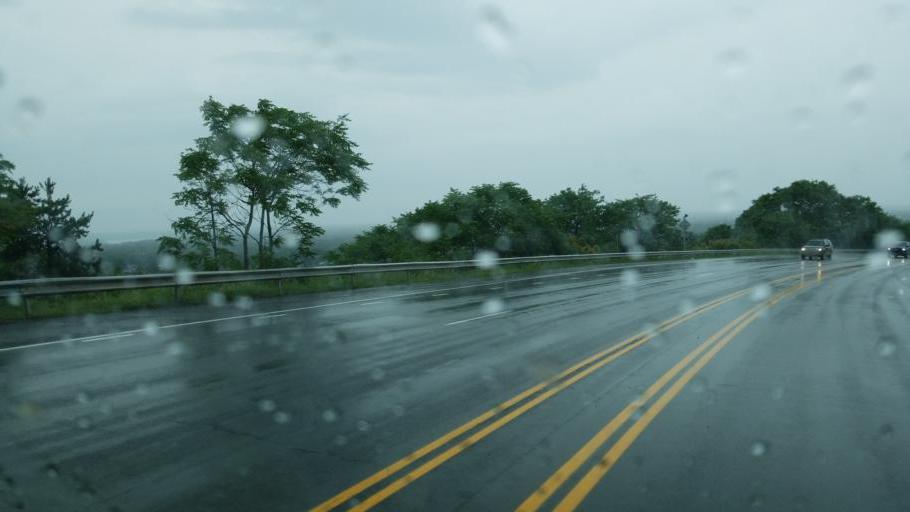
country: US
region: New York
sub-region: Niagara County
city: Lewiston
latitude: 43.1640
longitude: -79.0373
